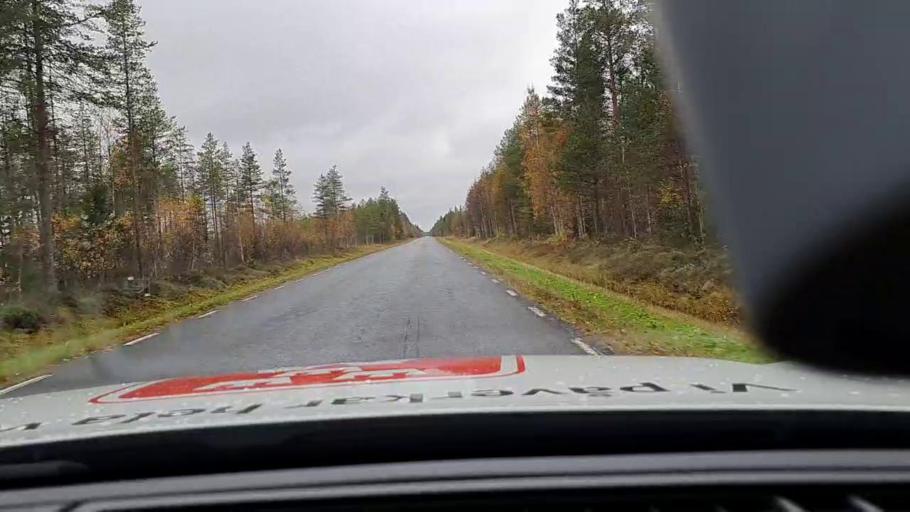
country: SE
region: Norrbotten
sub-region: Haparanda Kommun
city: Haparanda
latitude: 65.9069
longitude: 23.8320
